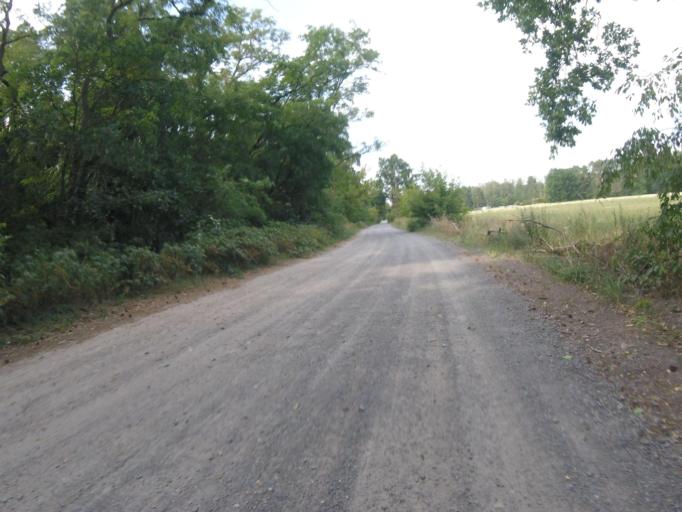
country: DE
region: Brandenburg
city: Wildau
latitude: 52.3103
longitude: 13.7186
